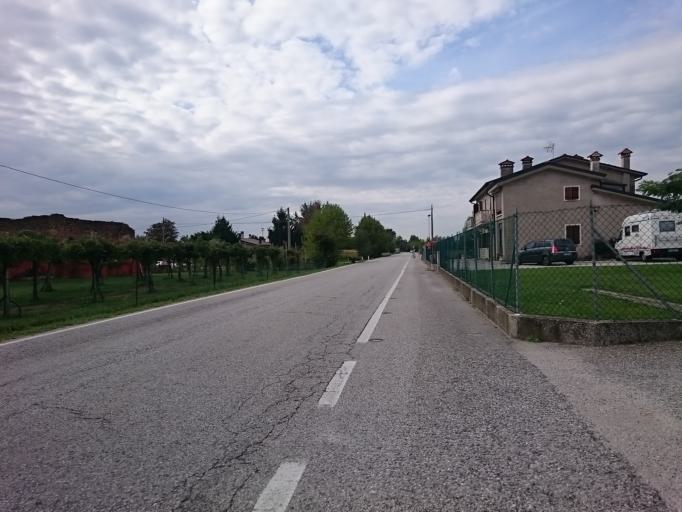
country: IT
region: Veneto
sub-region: Provincia di Vicenza
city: Grisignano di Zocco
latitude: 45.4876
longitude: 11.6950
